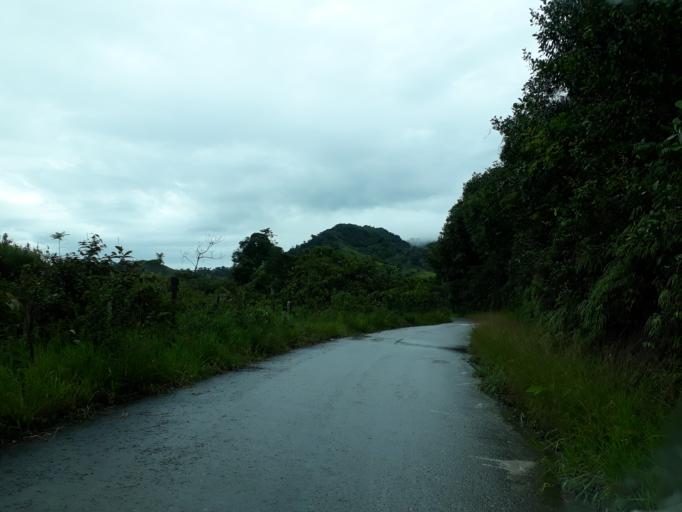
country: CO
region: Cundinamarca
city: Medina
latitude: 4.6766
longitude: -73.3220
